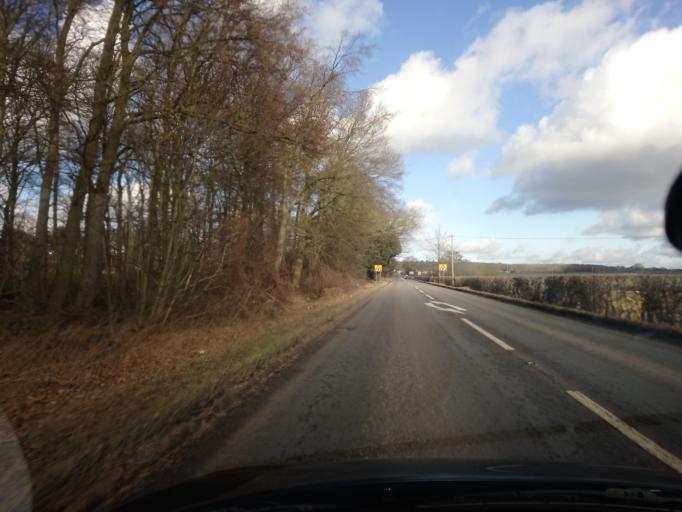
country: GB
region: England
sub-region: Shropshire
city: Clive
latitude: 52.7870
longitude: -2.7050
